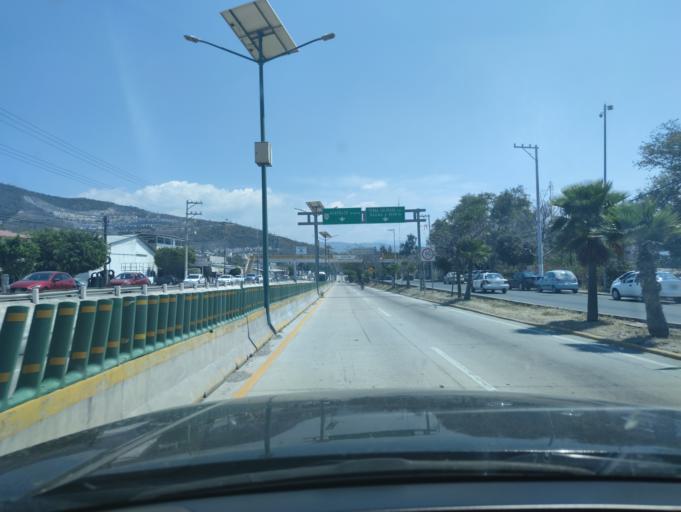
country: MX
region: Guerrero
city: Chilpancingo de los Bravos
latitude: 17.5242
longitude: -99.4870
